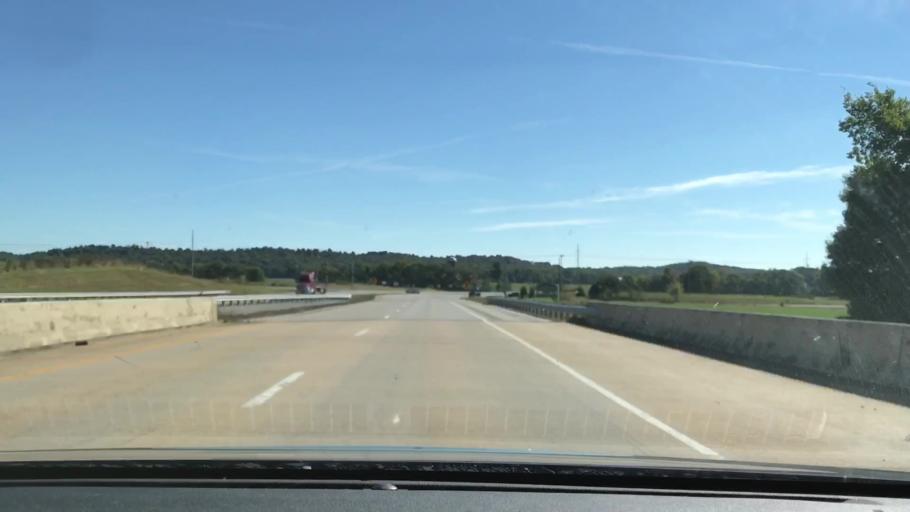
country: US
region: Kentucky
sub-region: Todd County
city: Elkton
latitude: 36.8244
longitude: -87.1541
